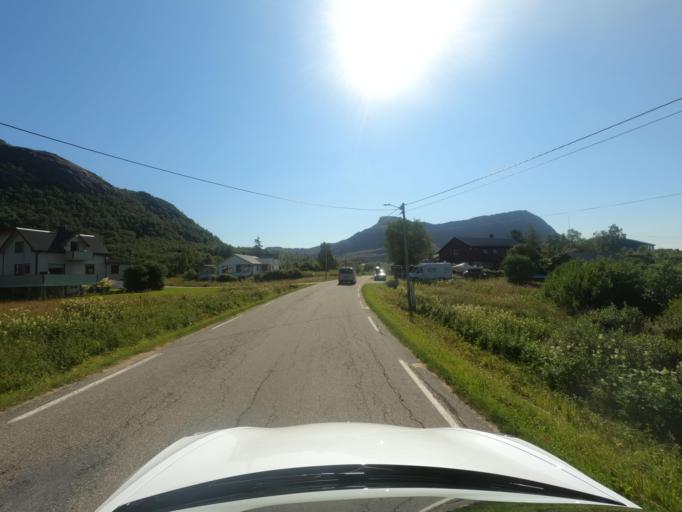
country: NO
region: Nordland
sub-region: Hadsel
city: Stokmarknes
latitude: 68.3094
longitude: 14.9926
